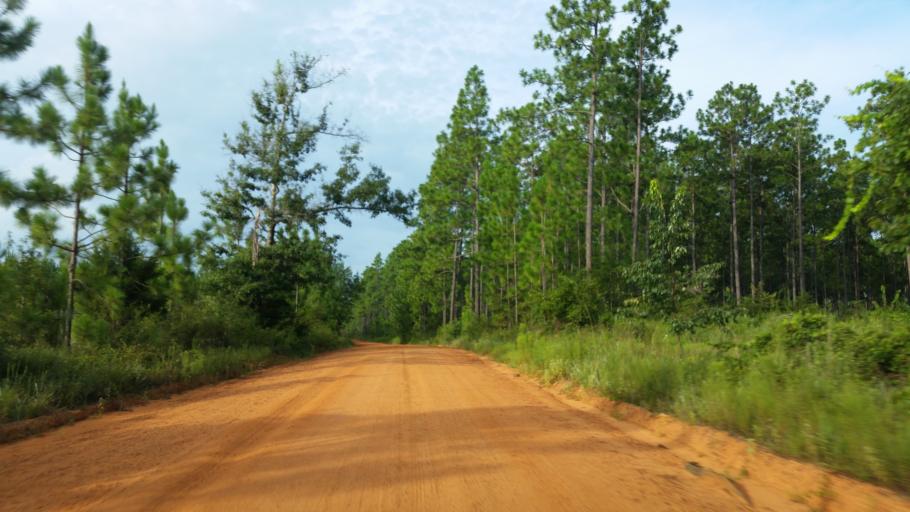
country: US
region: Alabama
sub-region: Escambia County
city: Atmore
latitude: 30.9173
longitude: -87.5781
